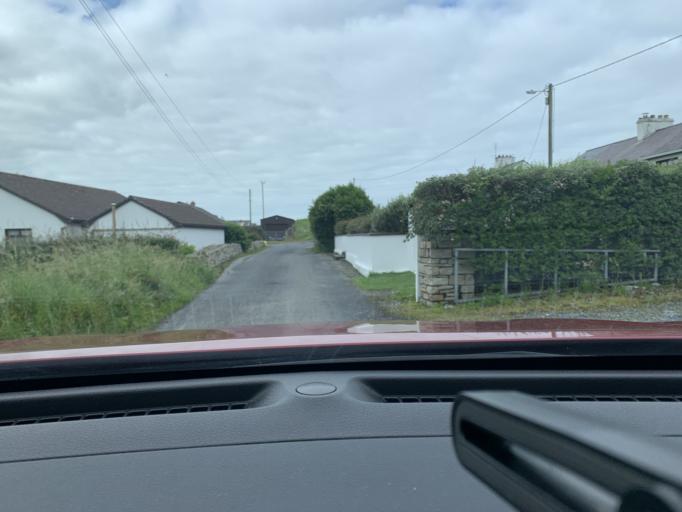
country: IE
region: Ulster
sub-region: County Donegal
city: Killybegs
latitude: 54.4661
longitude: -8.4517
